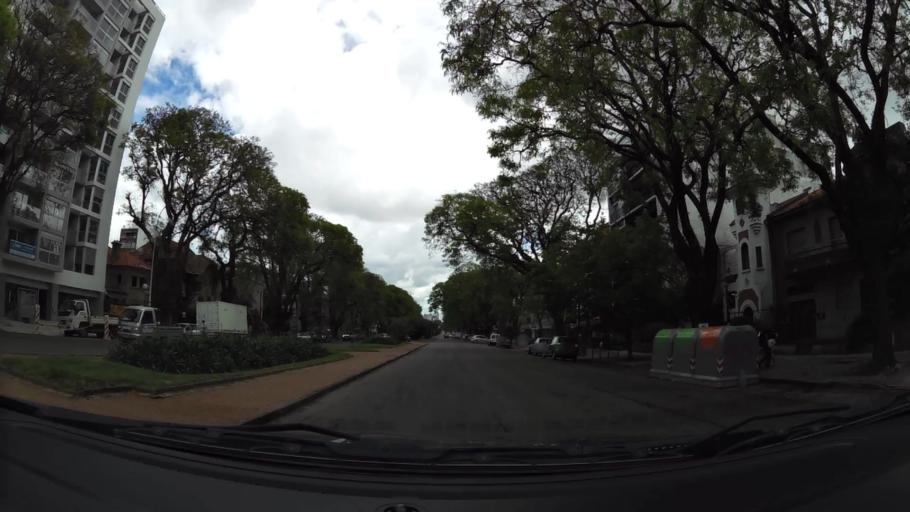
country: UY
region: Montevideo
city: Montevideo
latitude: -34.9192
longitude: -56.1622
